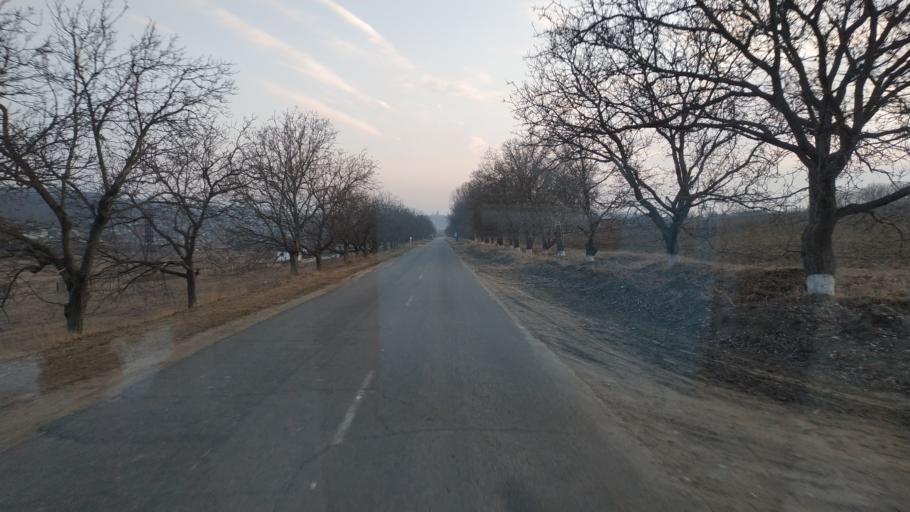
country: MD
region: Hincesti
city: Dancu
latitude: 46.6820
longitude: 28.3354
